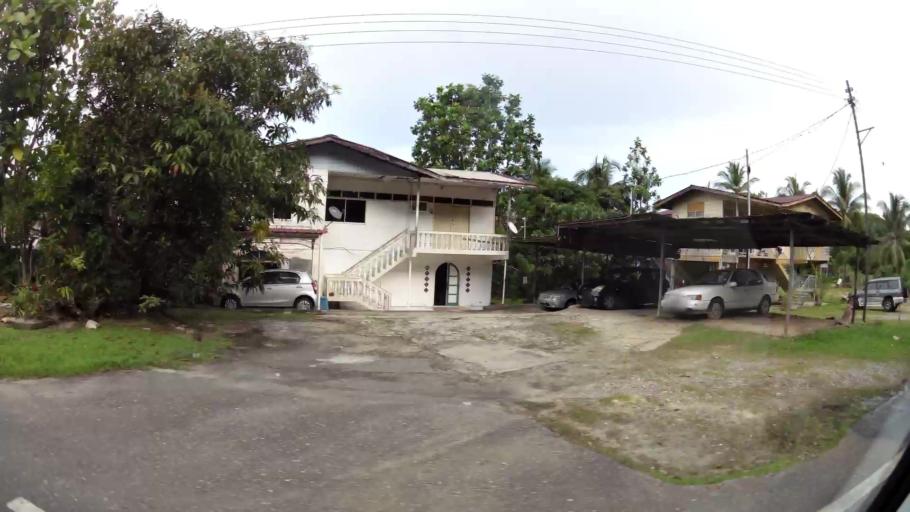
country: BN
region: Brunei and Muara
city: Bandar Seri Begawan
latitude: 4.9314
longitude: 115.0160
